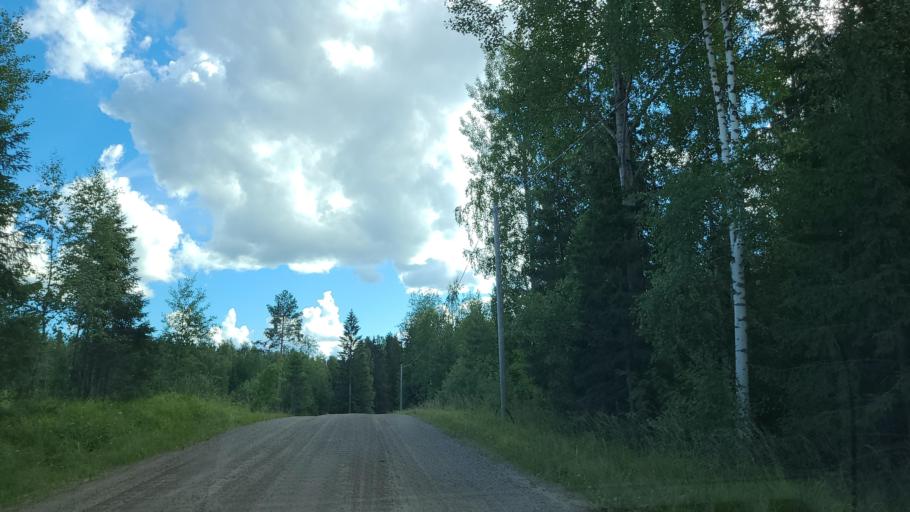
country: FI
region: Central Finland
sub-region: Jaemsae
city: Jaemsae
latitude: 61.9166
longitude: 25.3052
